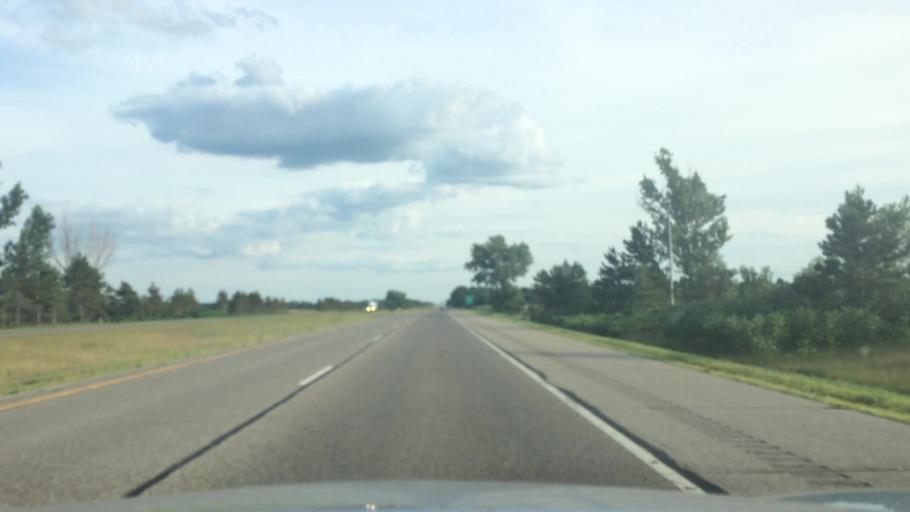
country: US
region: Wisconsin
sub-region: Portage County
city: Plover
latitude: 44.2814
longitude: -89.5237
